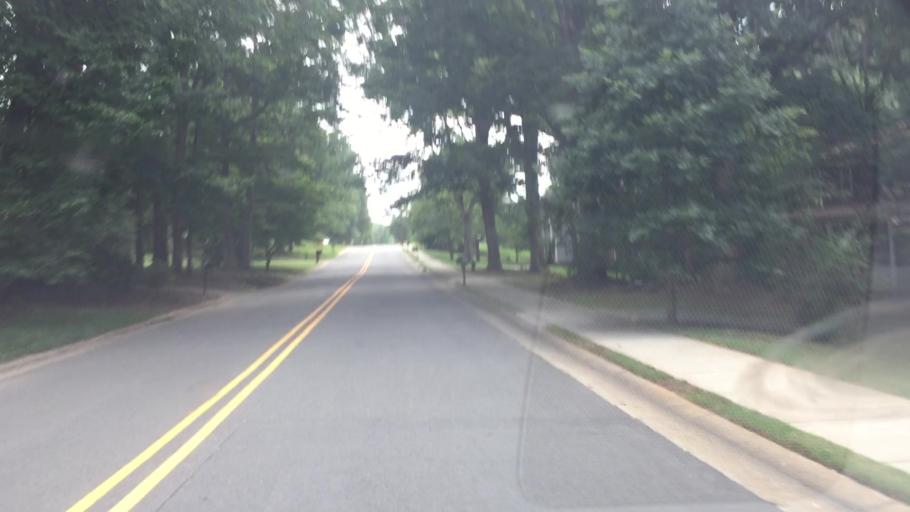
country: US
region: North Carolina
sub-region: Iredell County
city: Mooresville
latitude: 35.5564
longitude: -80.8015
